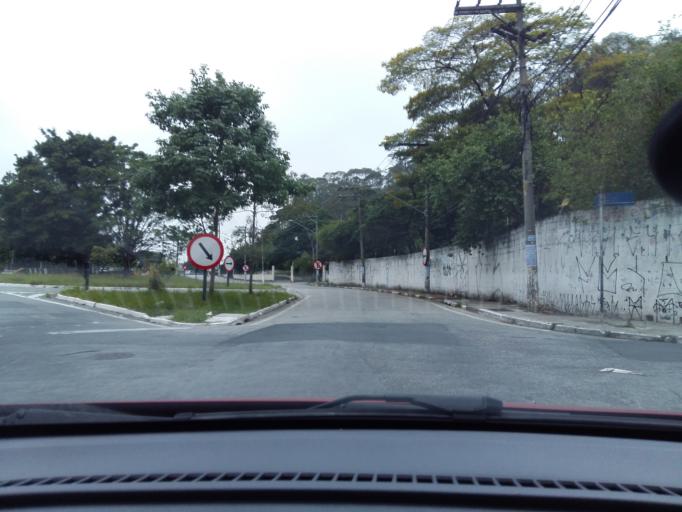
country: BR
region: Sao Paulo
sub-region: Sao Caetano Do Sul
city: Sao Caetano do Sul
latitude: -23.6398
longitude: -46.5922
